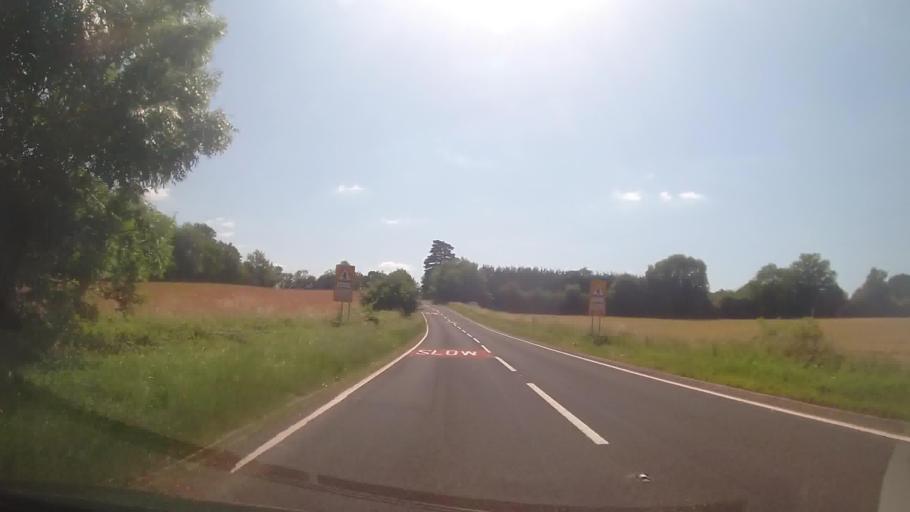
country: GB
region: England
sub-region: Herefordshire
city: Ocle Pychard
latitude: 52.0946
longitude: -2.5762
